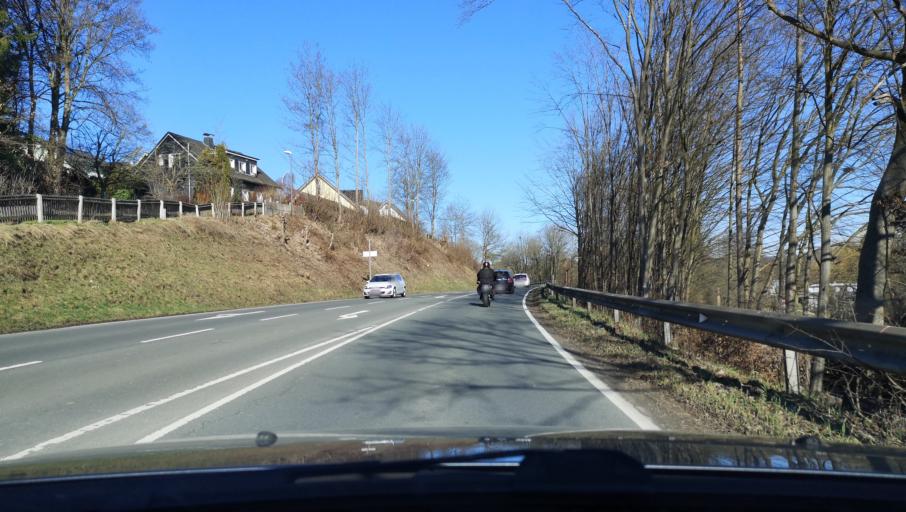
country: DE
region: North Rhine-Westphalia
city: Wipperfurth
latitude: 51.1209
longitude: 7.3993
